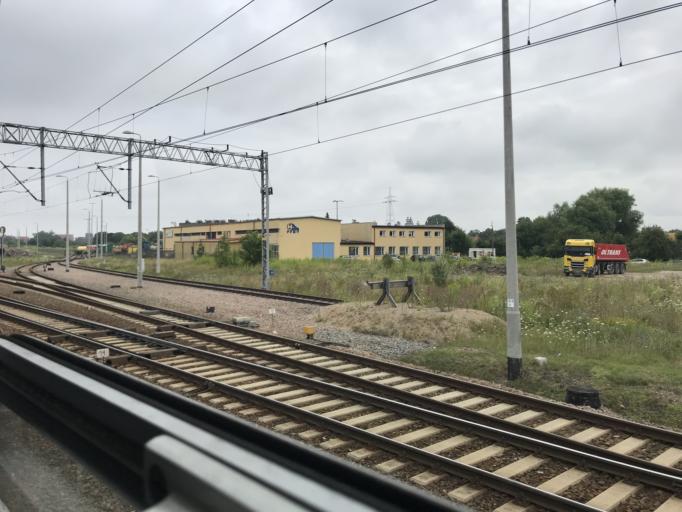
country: PL
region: Pomeranian Voivodeship
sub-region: Gdansk
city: Gdansk
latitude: 54.3324
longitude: 18.6379
